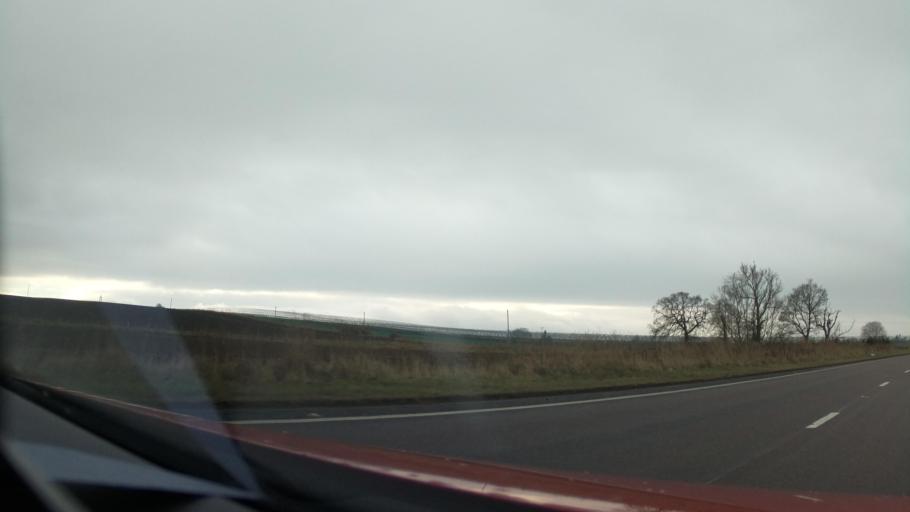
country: GB
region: Scotland
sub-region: Perth and Kinross
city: Errol
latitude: 56.3922
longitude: -3.2751
